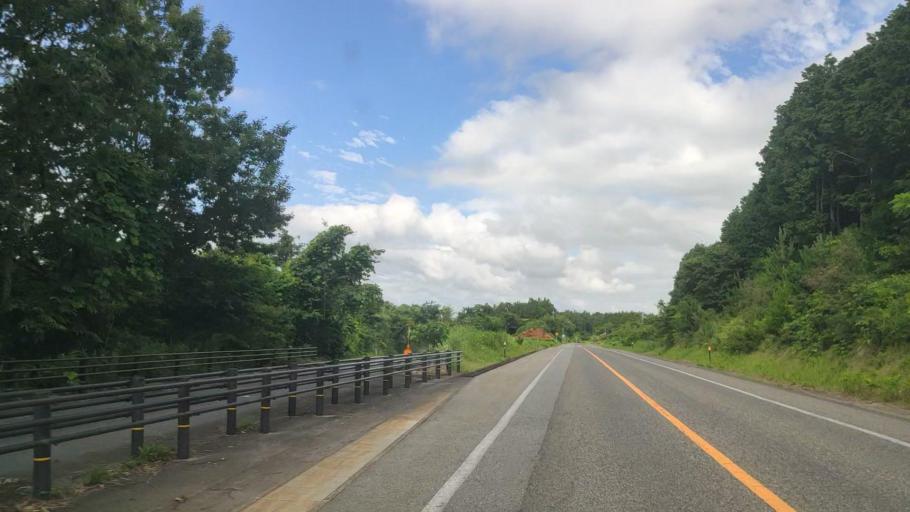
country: JP
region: Tottori
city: Yonago
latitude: 35.4181
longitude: 133.4521
